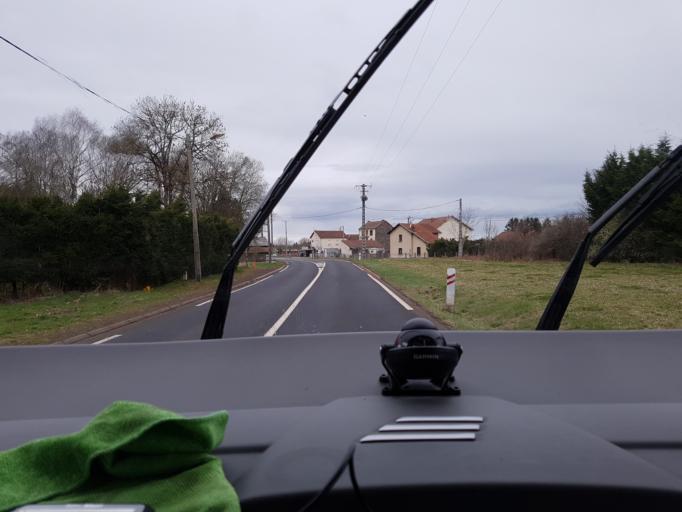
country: FR
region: Auvergne
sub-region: Departement du Puy-de-Dome
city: Saint-Ours
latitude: 45.8589
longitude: 2.9194
